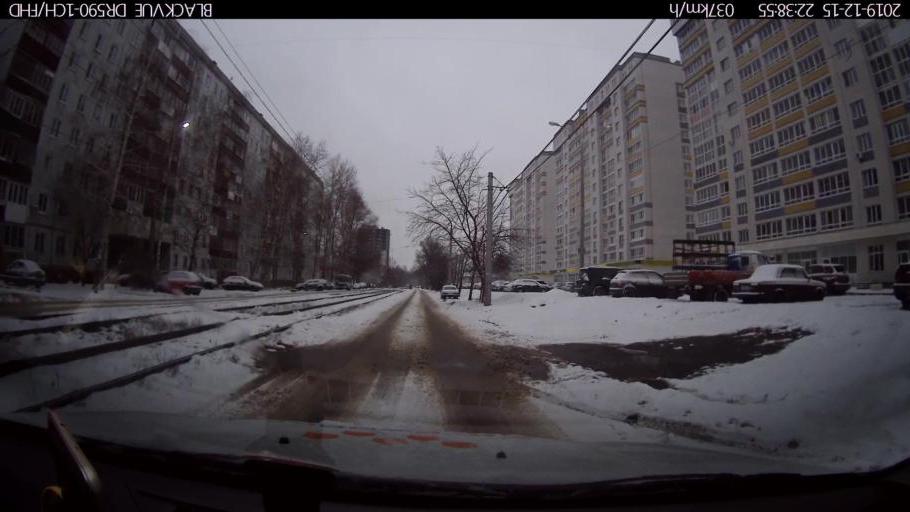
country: RU
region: Nizjnij Novgorod
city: Gorbatovka
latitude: 56.3420
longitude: 43.8377
